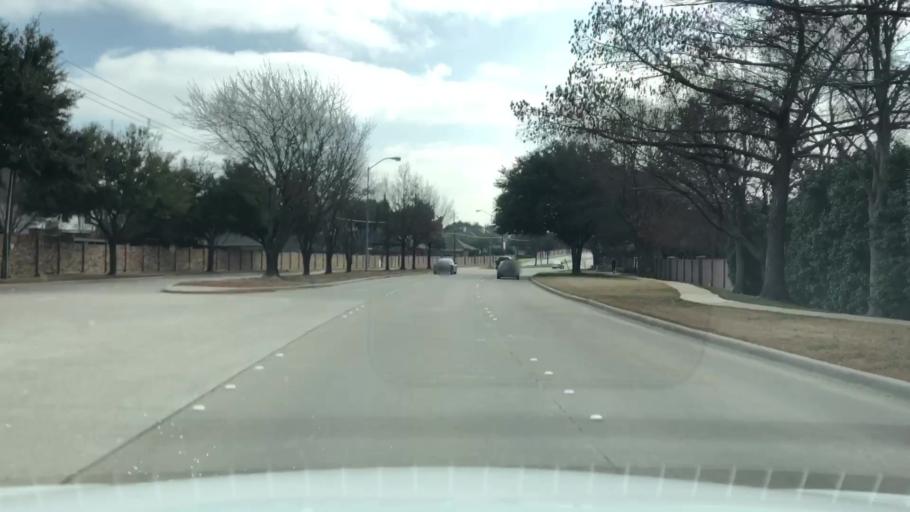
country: US
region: Texas
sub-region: Denton County
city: The Colony
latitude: 33.0400
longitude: -96.8387
